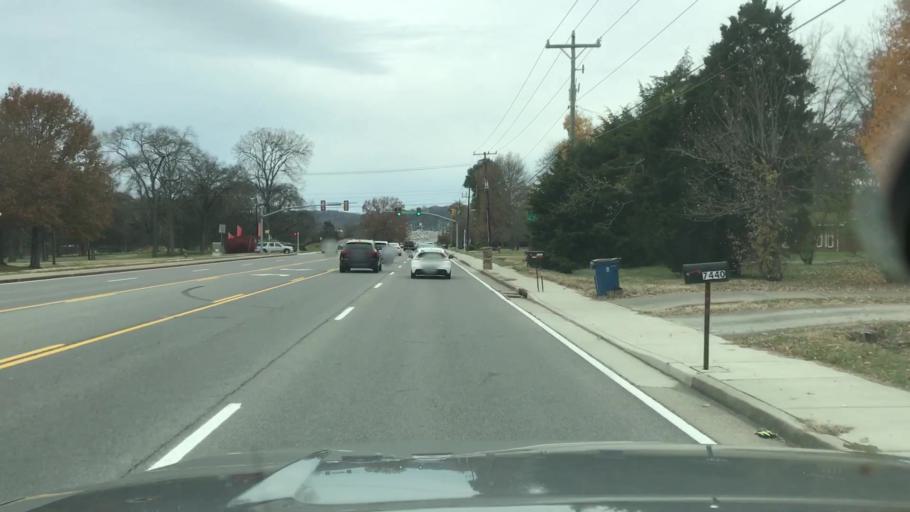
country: US
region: Tennessee
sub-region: Davidson County
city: Belle Meade
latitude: 36.0751
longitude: -86.9389
